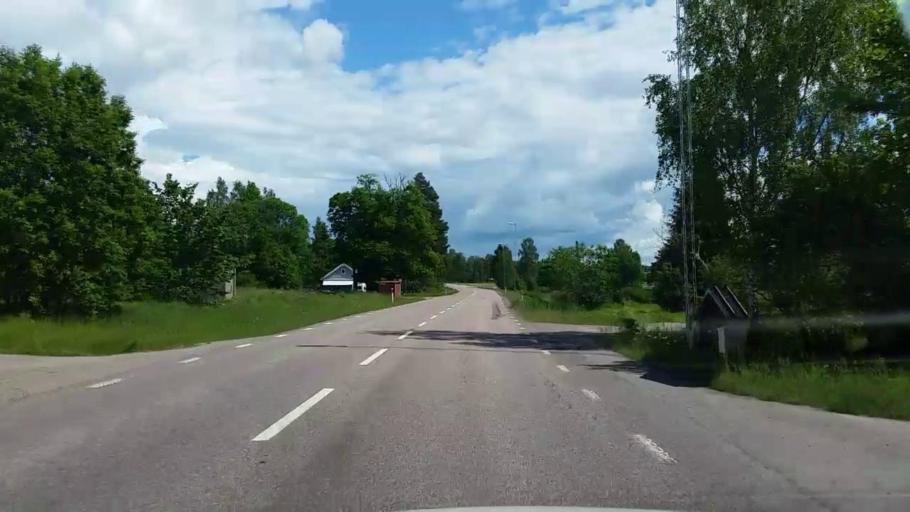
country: SE
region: Dalarna
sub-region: Avesta Kommun
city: Avesta
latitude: 60.1578
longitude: 16.2573
